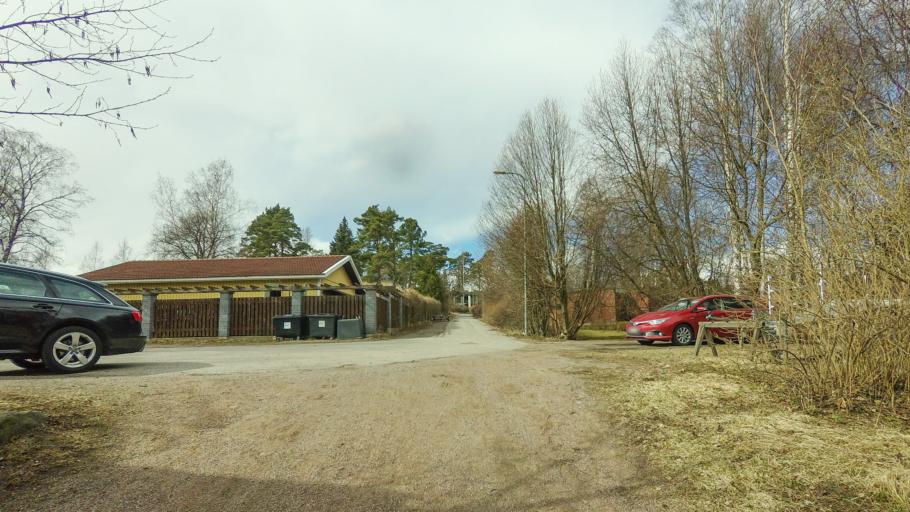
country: FI
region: Uusimaa
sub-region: Helsinki
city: Vantaa
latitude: 60.2011
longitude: 25.0971
